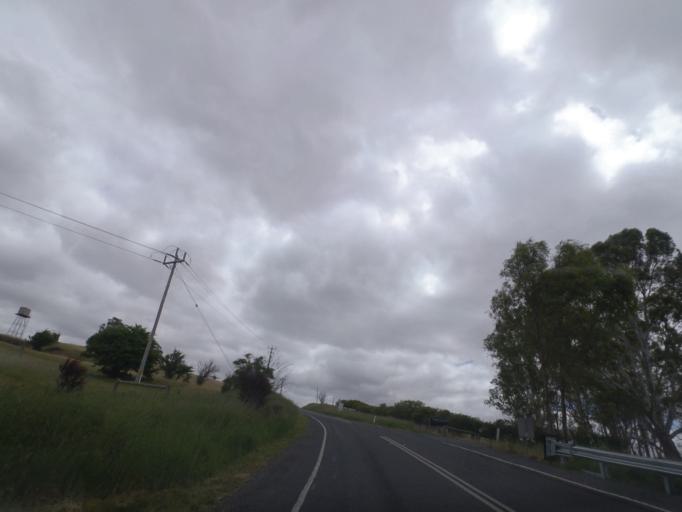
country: AU
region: Victoria
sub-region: Whittlesea
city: Whittlesea
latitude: -37.1892
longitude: 145.0390
